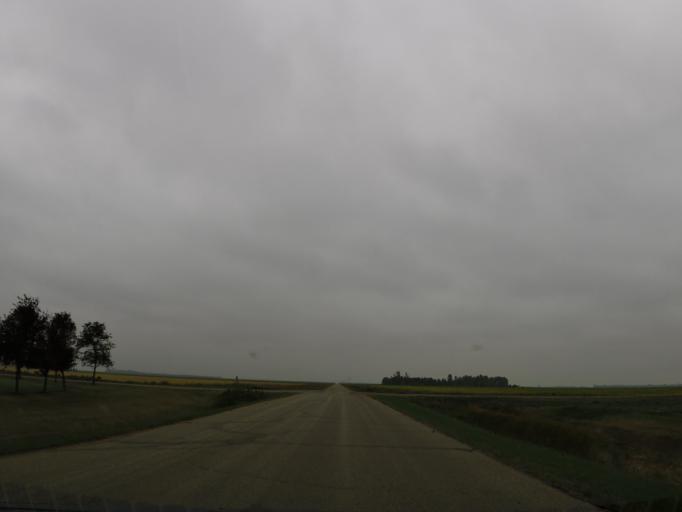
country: US
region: Minnesota
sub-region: Marshall County
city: Warren
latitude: 48.4468
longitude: -96.8892
